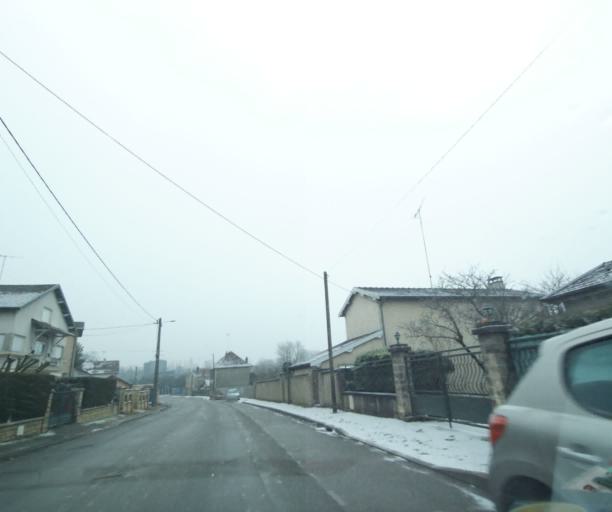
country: FR
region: Champagne-Ardenne
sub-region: Departement de la Haute-Marne
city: Wassy
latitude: 48.4946
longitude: 4.9543
